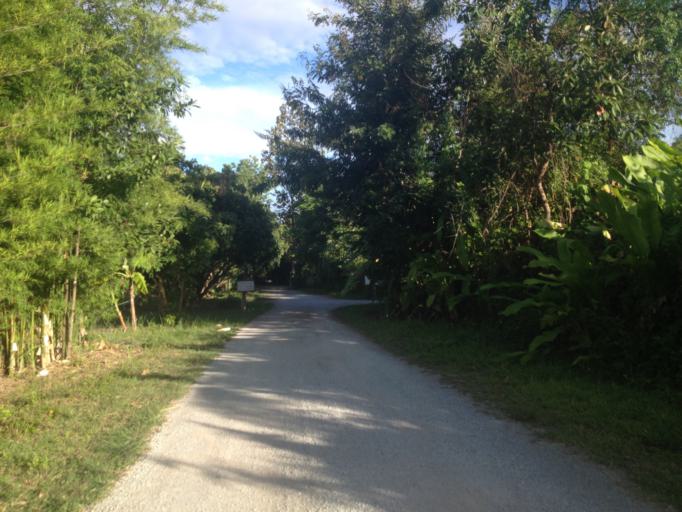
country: TH
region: Chiang Mai
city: Hang Dong
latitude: 18.6936
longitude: 98.8912
